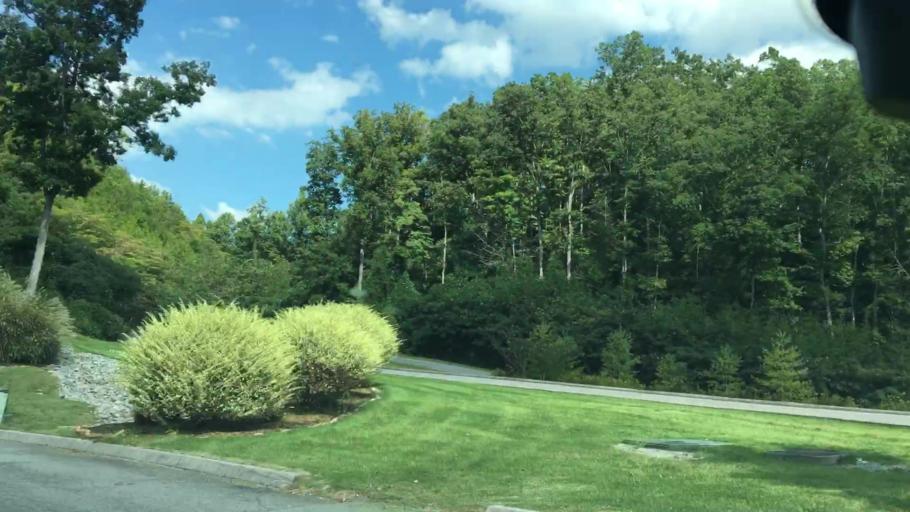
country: US
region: Tennessee
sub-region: Sevier County
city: Gatlinburg
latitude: 35.7306
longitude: -83.4817
